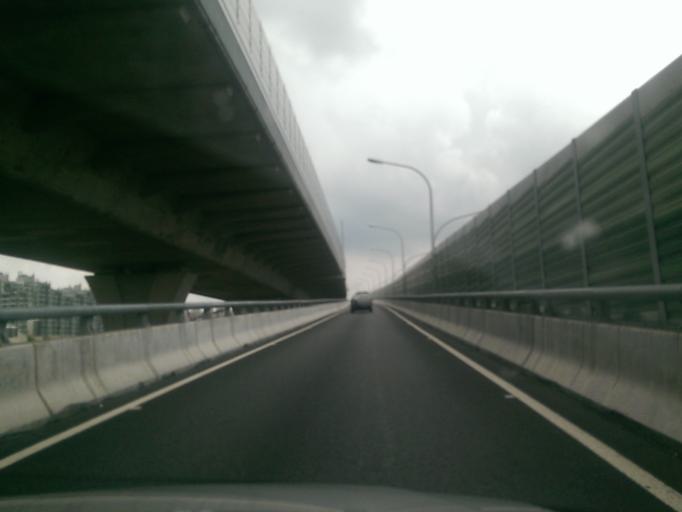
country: TW
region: Taiwan
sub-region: Taichung City
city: Taichung
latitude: 24.1477
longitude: 120.7140
